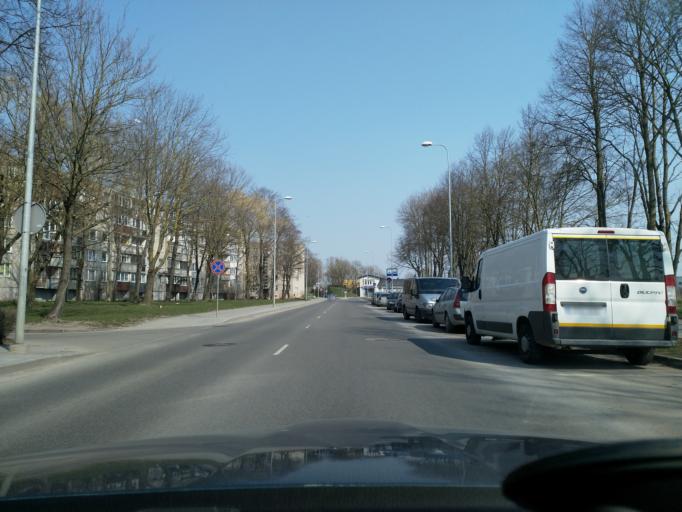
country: LT
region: Klaipedos apskritis
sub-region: Klaipeda
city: Klaipeda
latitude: 55.6990
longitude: 21.1646
